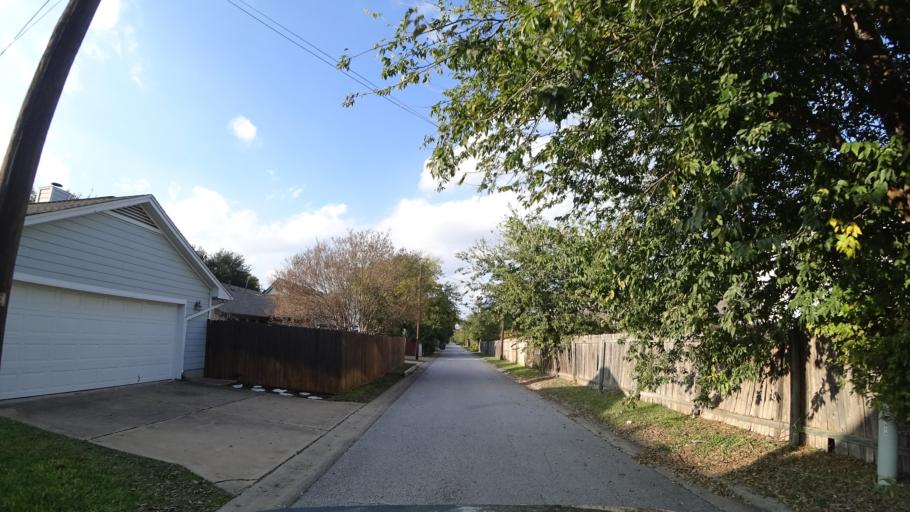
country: US
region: Texas
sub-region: Williamson County
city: Round Rock
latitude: 30.4923
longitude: -97.6634
